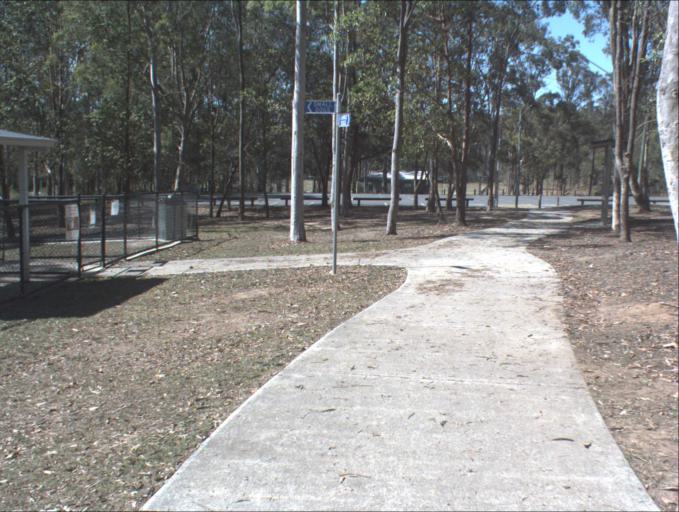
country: AU
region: Queensland
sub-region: Logan
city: Springwood
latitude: -27.5993
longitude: 153.1457
